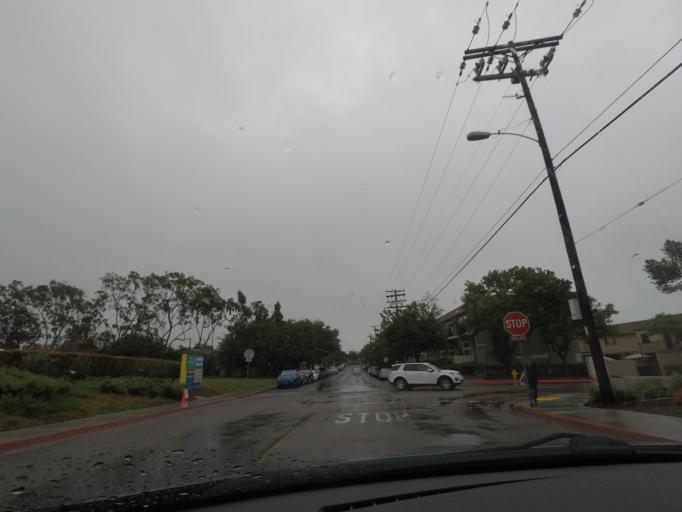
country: US
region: California
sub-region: San Diego County
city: San Diego
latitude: 32.7936
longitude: -117.1544
